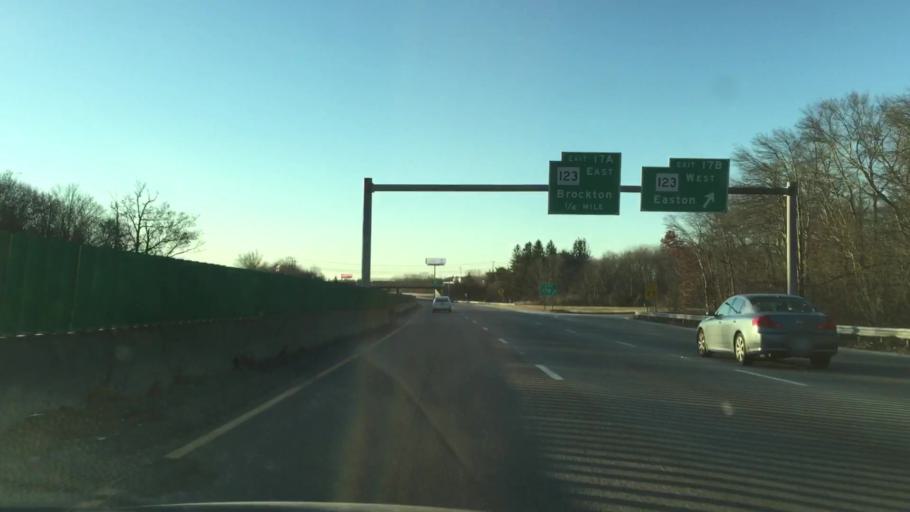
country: US
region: Massachusetts
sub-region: Plymouth County
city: Brockton
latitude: 42.0652
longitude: -71.0621
